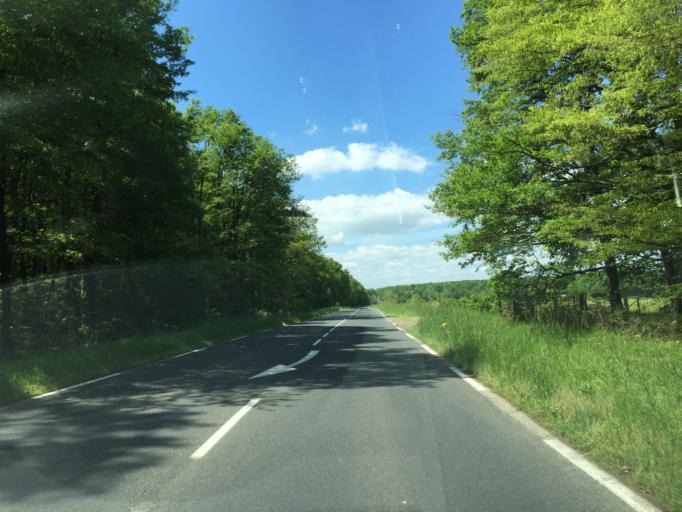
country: FR
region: Auvergne
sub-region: Departement de l'Allier
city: Bellerive-sur-Allier
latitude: 46.1088
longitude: 3.3797
